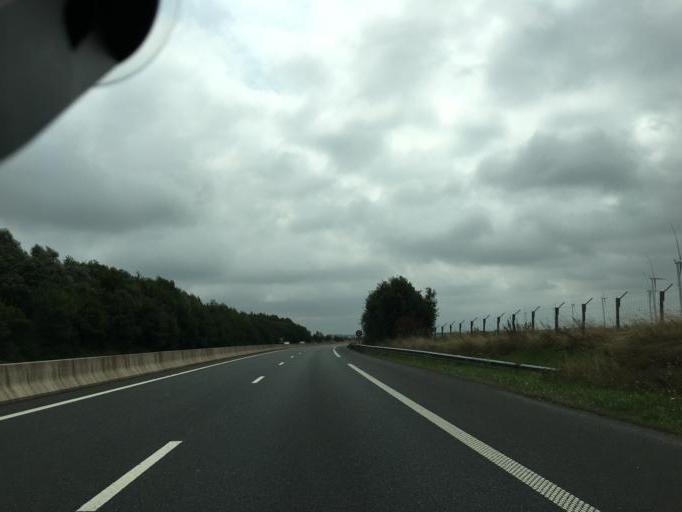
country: FR
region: Nord-Pas-de-Calais
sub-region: Departement du Pas-de-Calais
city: Campagne-les-Hesdin
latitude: 50.4079
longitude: 1.8359
